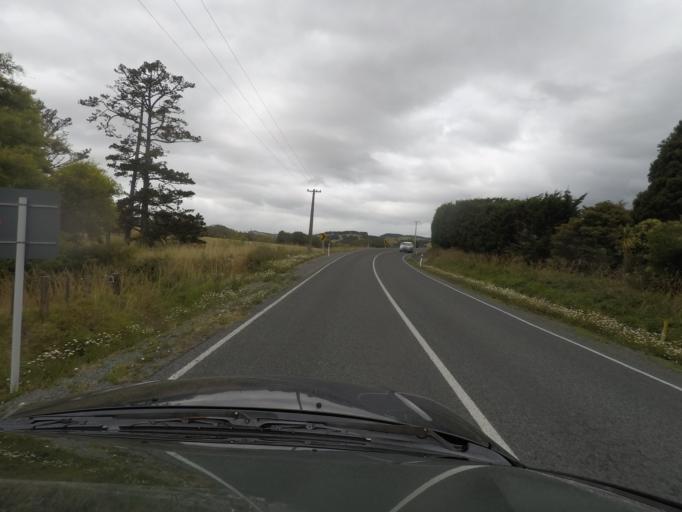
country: NZ
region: Auckland
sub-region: Auckland
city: Wellsford
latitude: -36.2826
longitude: 174.5611
